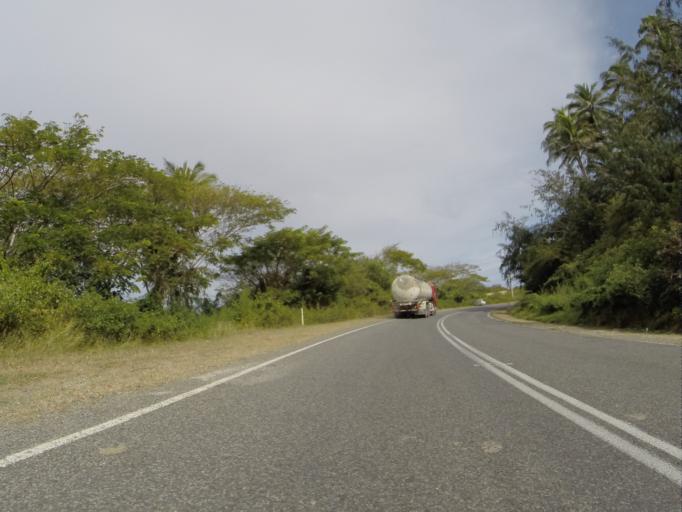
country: FJ
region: Western
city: Nadi
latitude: -18.1819
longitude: 177.5853
